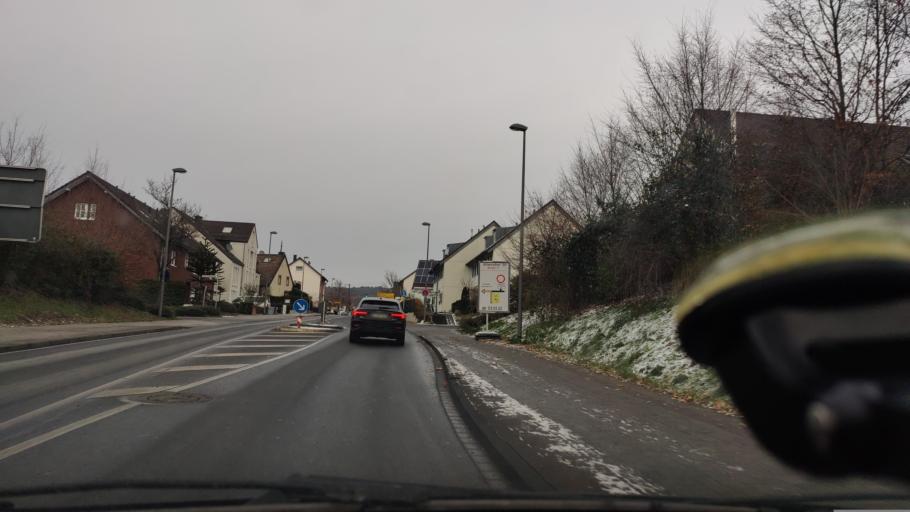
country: DE
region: North Rhine-Westphalia
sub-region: Regierungsbezirk Koln
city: Troisdorf
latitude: 50.8233
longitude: 7.1247
